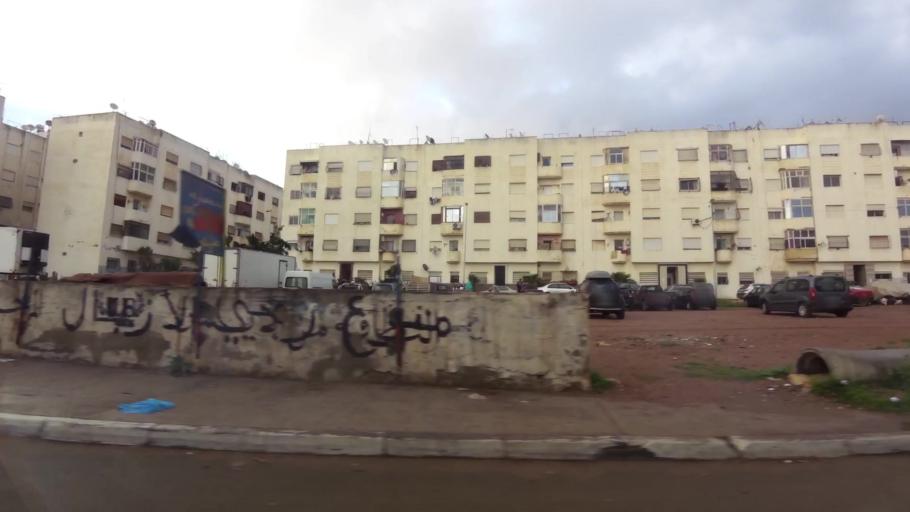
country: MA
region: Grand Casablanca
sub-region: Casablanca
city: Casablanca
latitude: 33.5382
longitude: -7.6853
